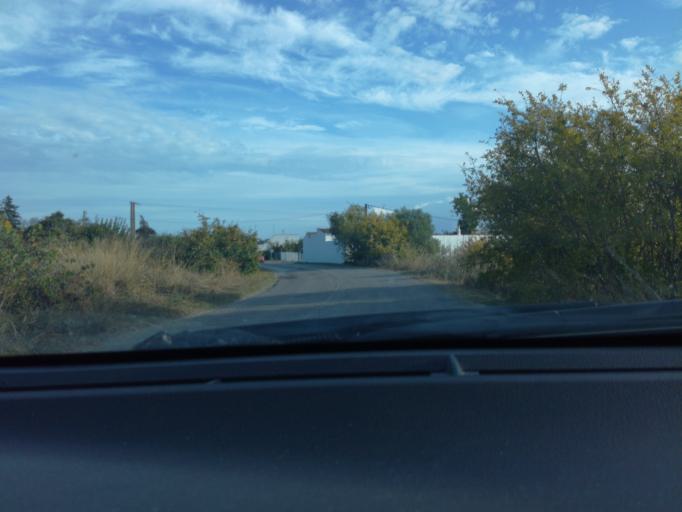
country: PT
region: Faro
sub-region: Olhao
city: Laranjeiro
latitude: 37.0682
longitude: -7.7671
